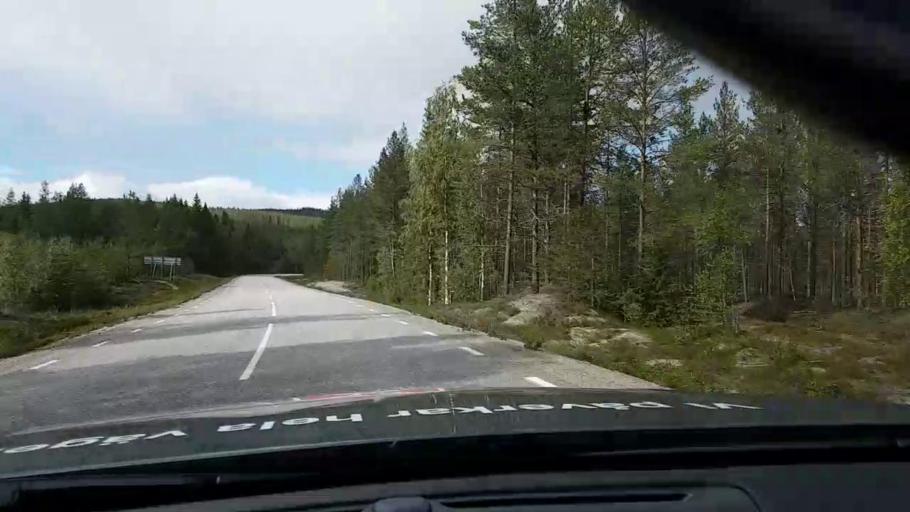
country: SE
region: Vaesternorrland
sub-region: OErnskoeldsviks Kommun
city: Bredbyn
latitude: 63.6847
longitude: 17.7765
